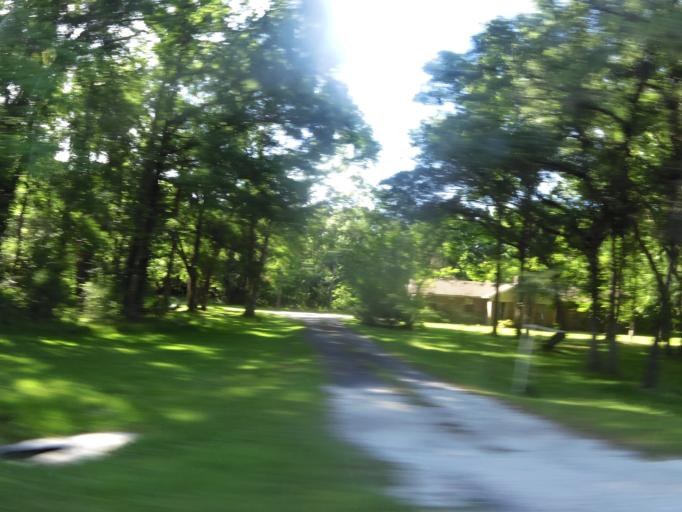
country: US
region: Florida
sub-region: Nassau County
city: Nassau Village-Ratliff
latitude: 30.5005
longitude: -81.8094
